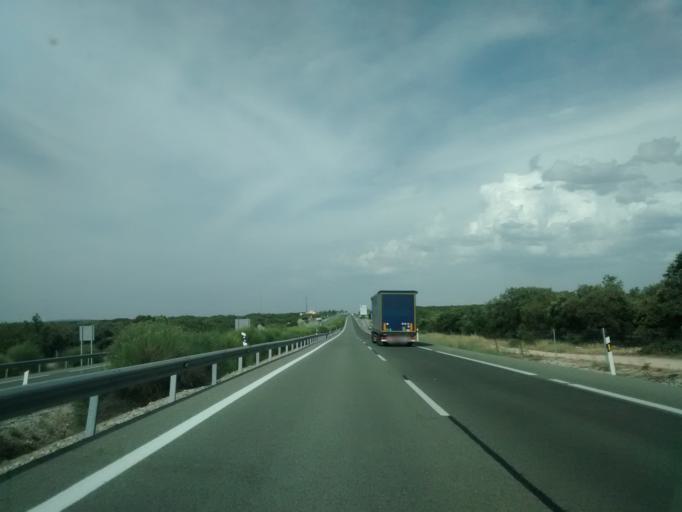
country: ES
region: Castille-La Mancha
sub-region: Provincia de Guadalajara
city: Sauca
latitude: 41.0060
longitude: -2.5666
